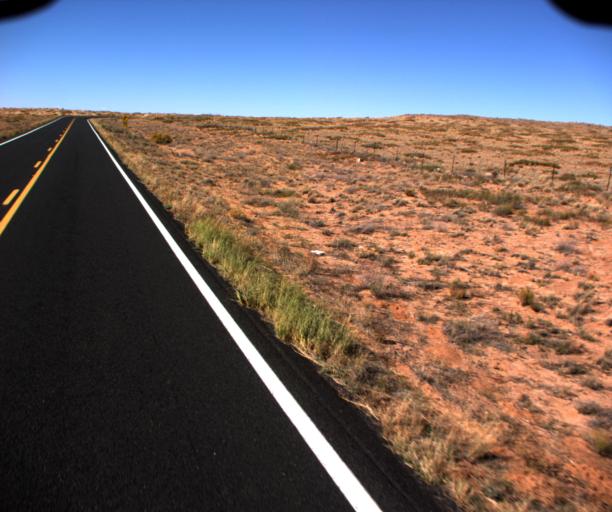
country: US
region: Arizona
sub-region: Coconino County
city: Tuba City
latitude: 36.0355
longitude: -111.1815
